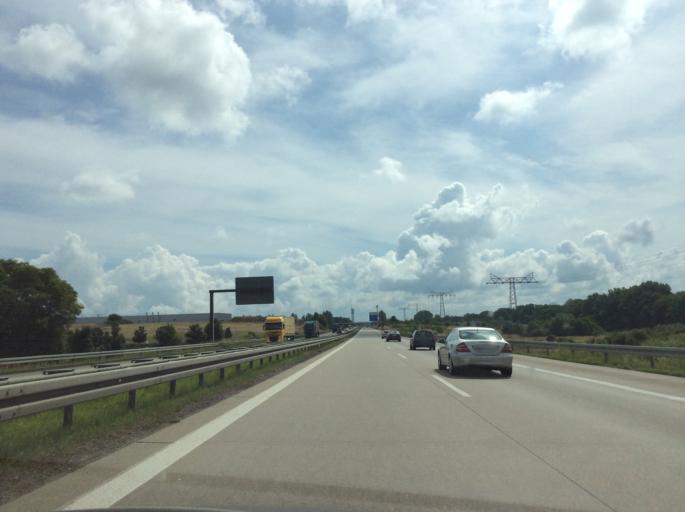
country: DE
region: Brandenburg
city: Frankfurt (Oder)
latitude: 52.3203
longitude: 14.4881
